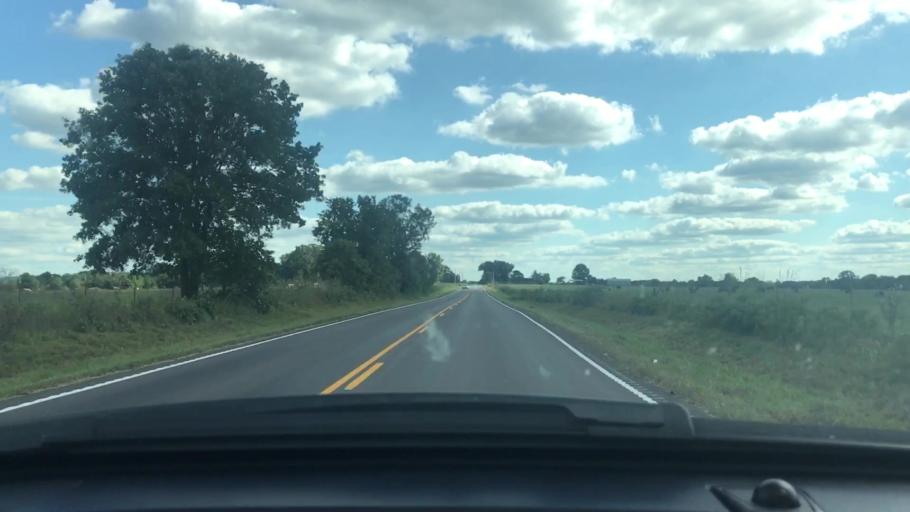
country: US
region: Missouri
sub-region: Wright County
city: Mountain Grove
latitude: 37.2683
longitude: -92.3081
